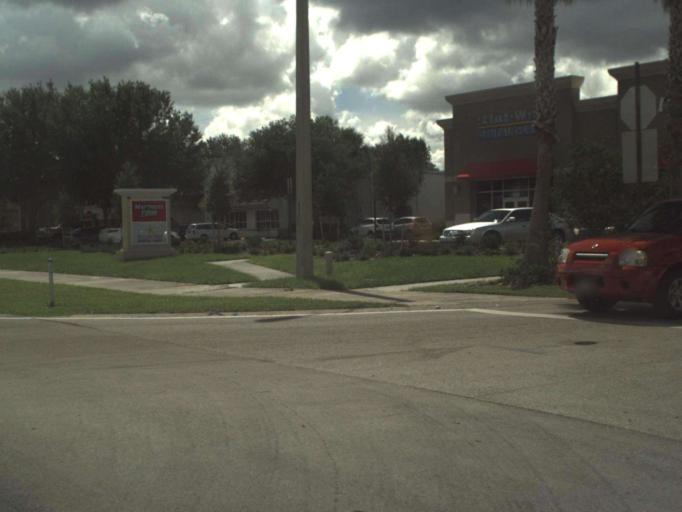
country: US
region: Florida
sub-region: Saint Lucie County
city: River Park
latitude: 27.3155
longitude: -80.3902
